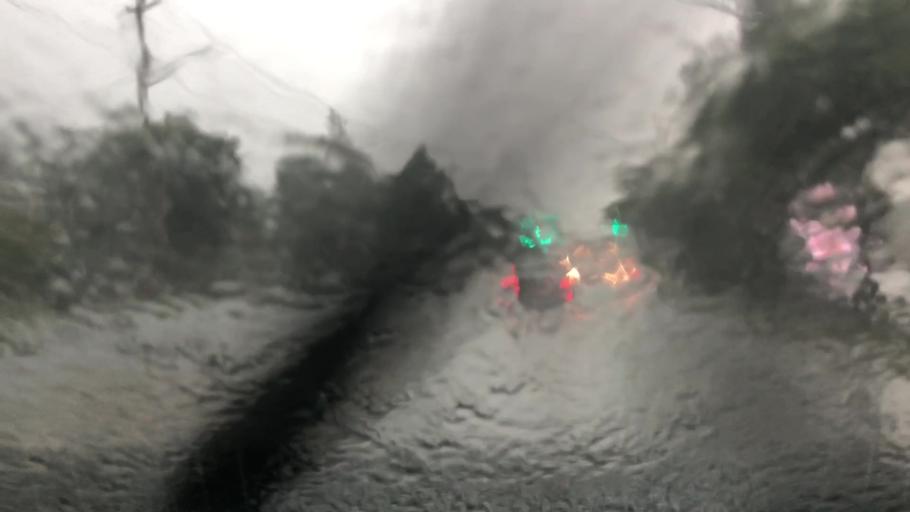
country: US
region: New York
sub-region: Nassau County
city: North Merrick
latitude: 40.6942
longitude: -73.5781
